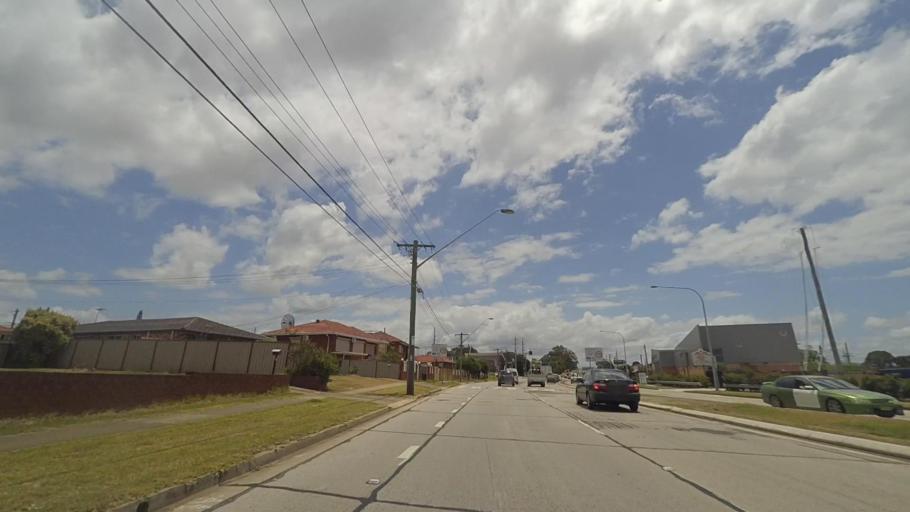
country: AU
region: New South Wales
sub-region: Fairfield
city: Cabramatta West
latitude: -33.8894
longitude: 150.9228
